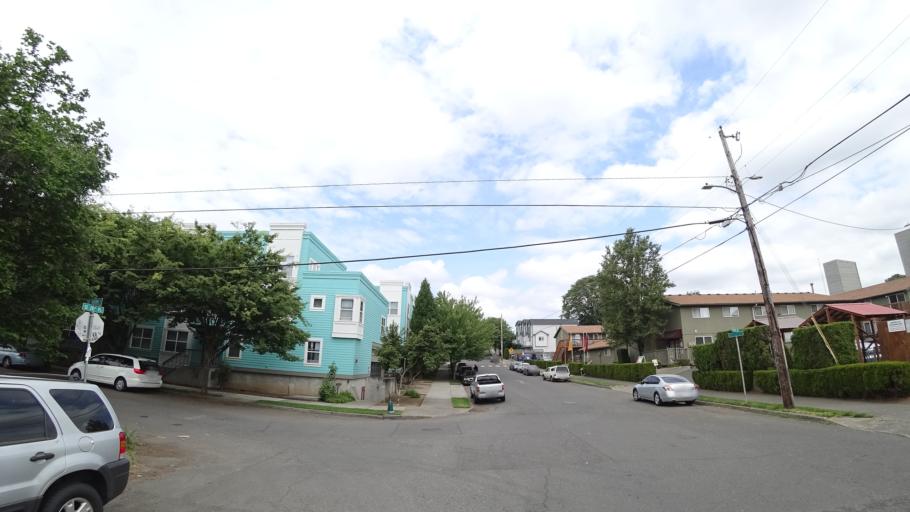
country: US
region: Oregon
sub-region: Multnomah County
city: Portland
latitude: 45.4960
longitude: -122.6368
